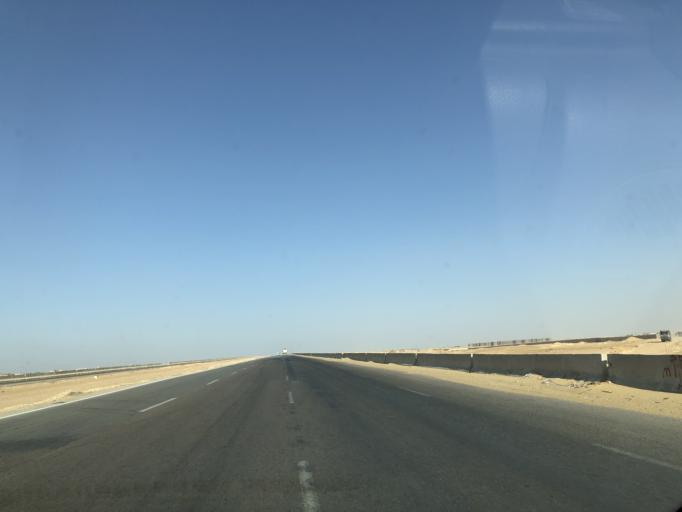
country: EG
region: Muhafazat al Minufiyah
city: Ashmun
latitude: 30.0675
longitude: 30.8621
